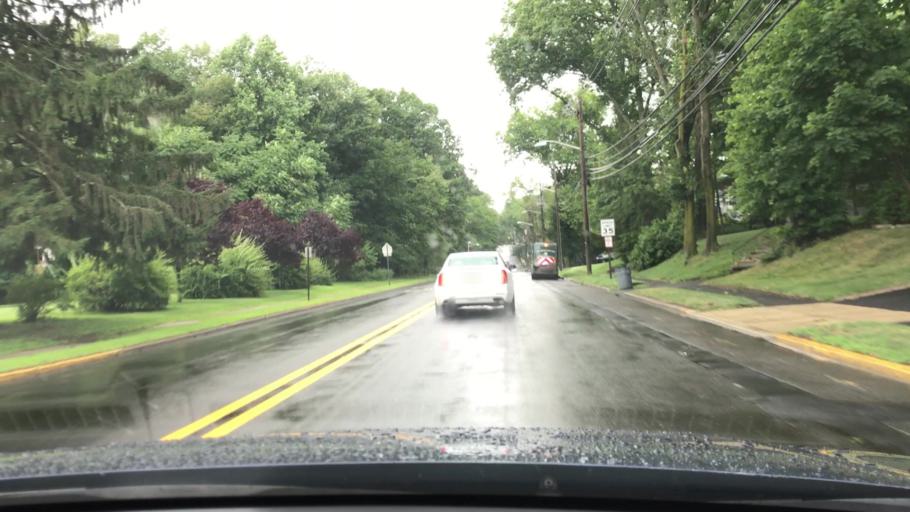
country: US
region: New Jersey
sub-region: Bergen County
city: Oradell
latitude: 40.9552
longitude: -74.0354
